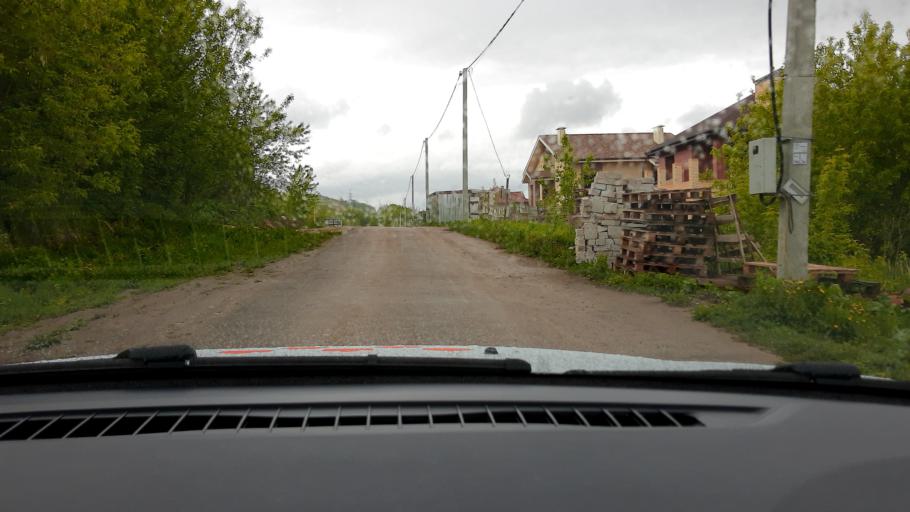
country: RU
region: Nizjnij Novgorod
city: Afonino
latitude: 56.2694
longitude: 44.0989
